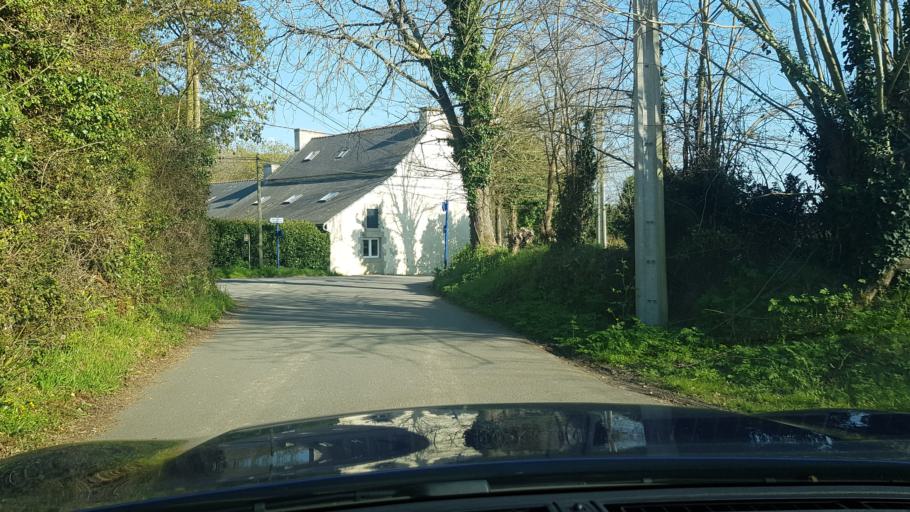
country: FR
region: Brittany
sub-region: Departement du Finistere
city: Clohars-Carnoet
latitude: 47.7773
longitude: -3.6140
